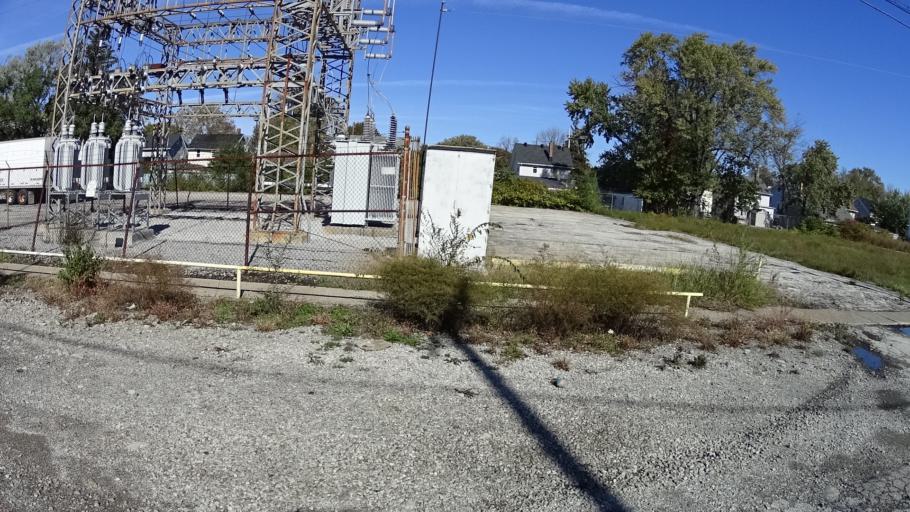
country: US
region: Ohio
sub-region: Lorain County
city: Lorain
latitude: 41.4571
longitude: -82.1836
